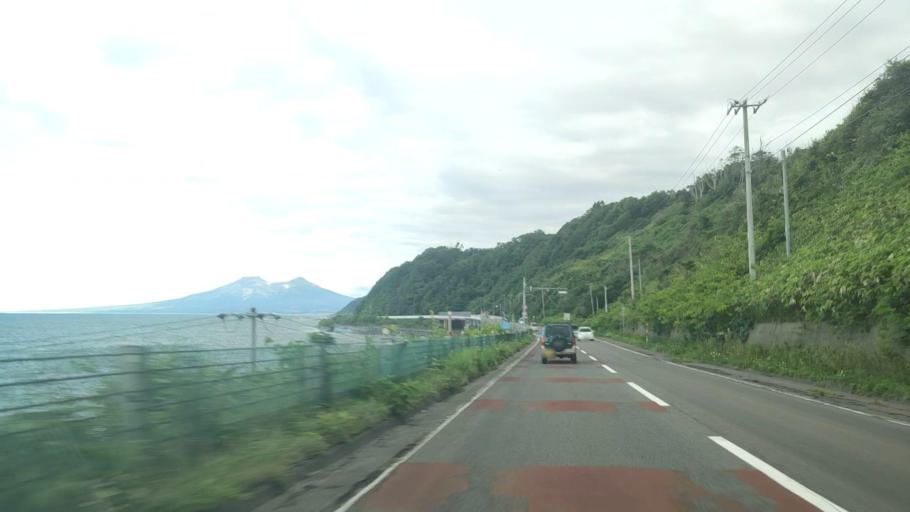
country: JP
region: Hokkaido
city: Nanae
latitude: 42.1669
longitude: 140.4619
